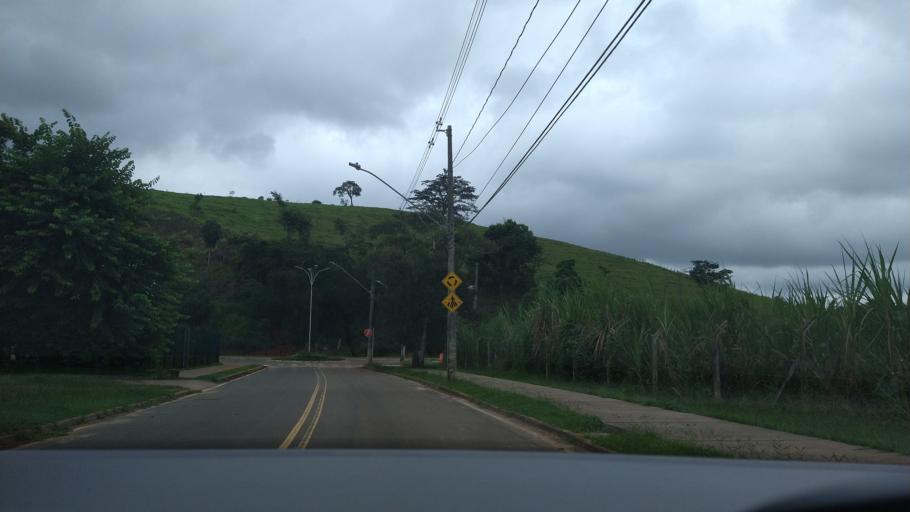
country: BR
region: Minas Gerais
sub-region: Vicosa
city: Vicosa
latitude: -20.7680
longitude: -42.8585
